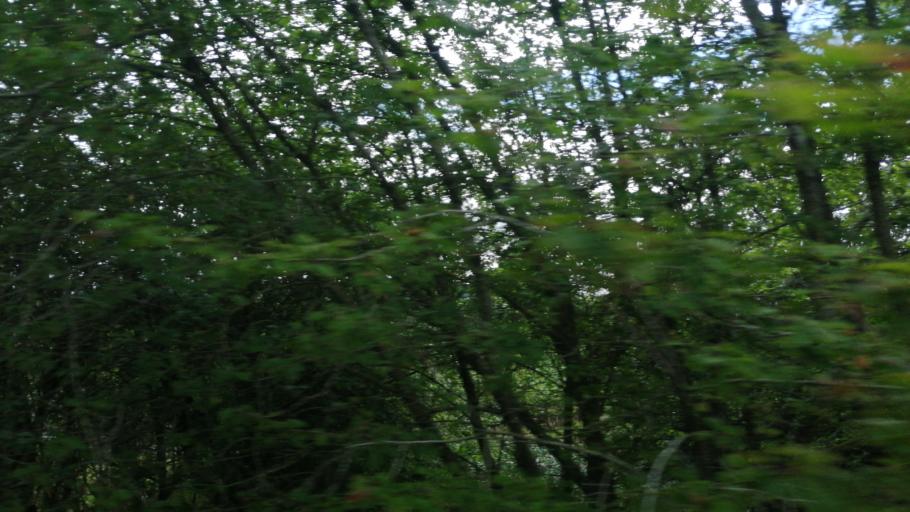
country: GB
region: Scotland
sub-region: Aberdeenshire
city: Insch
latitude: 57.3261
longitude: -2.5793
